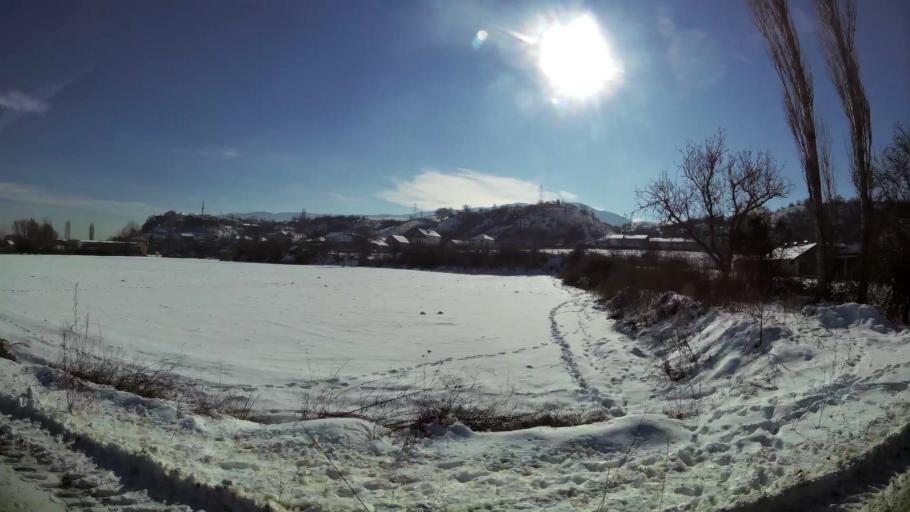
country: MK
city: Ljubin
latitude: 42.0046
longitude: 21.3020
